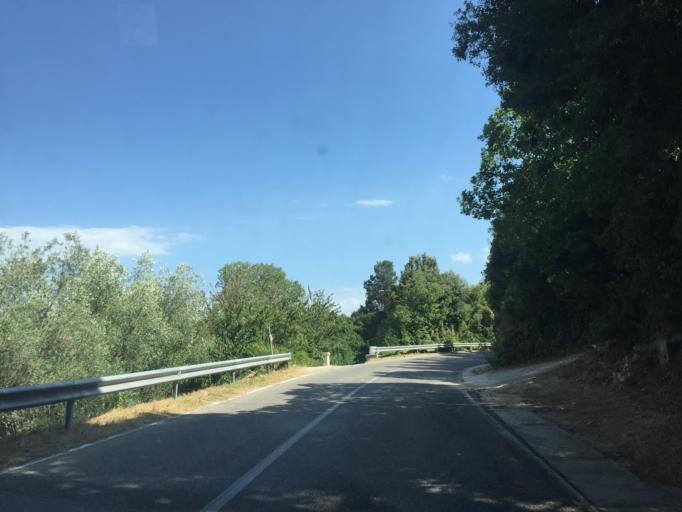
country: IT
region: Sardinia
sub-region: Provincia di Olbia-Tempio
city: Aggius
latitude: 40.9254
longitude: 9.0631
